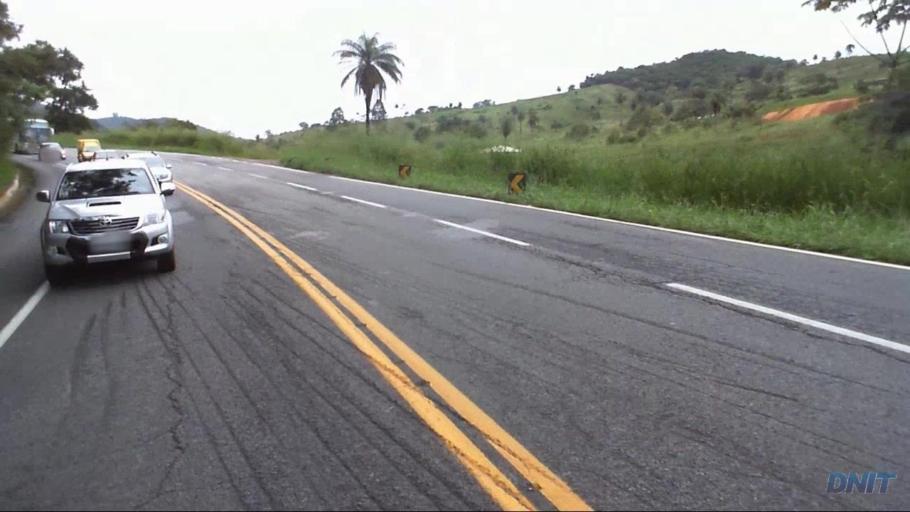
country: BR
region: Minas Gerais
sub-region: Joao Monlevade
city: Joao Monlevade
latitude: -19.8415
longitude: -43.3310
